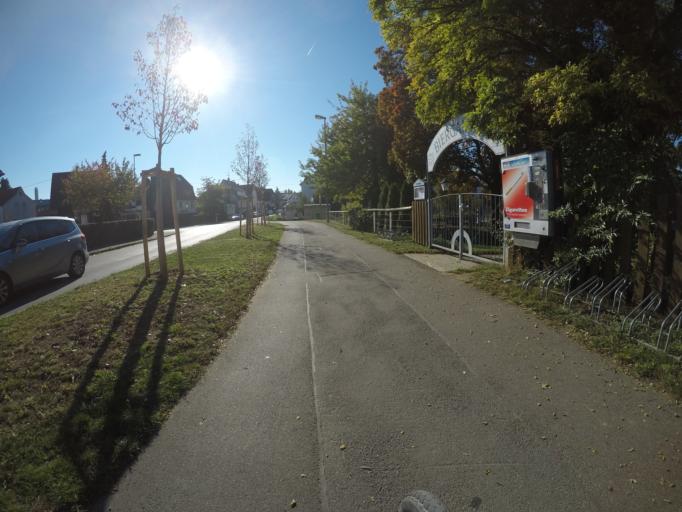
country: DE
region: Baden-Wuerttemberg
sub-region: Regierungsbezirk Stuttgart
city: Filderstadt
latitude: 48.6592
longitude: 9.2181
